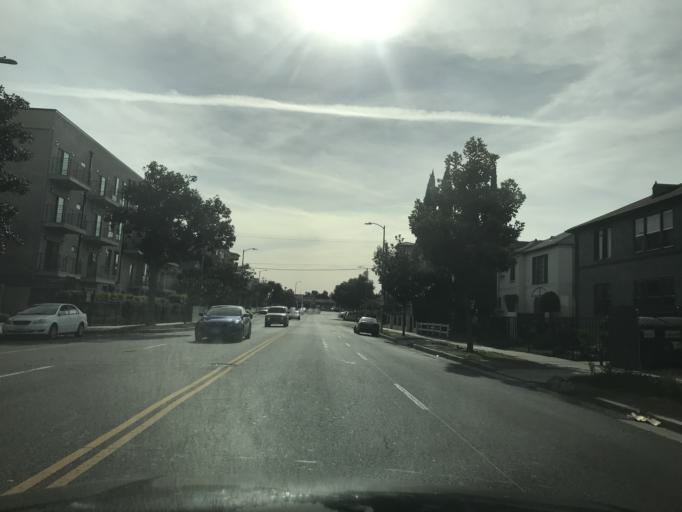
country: US
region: California
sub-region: Los Angeles County
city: Hollywood
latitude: 34.0552
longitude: -118.3143
